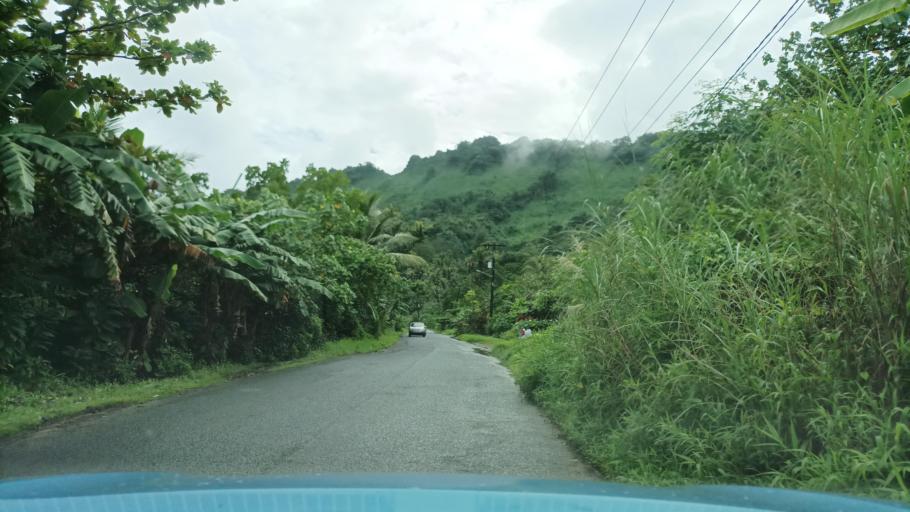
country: FM
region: Pohnpei
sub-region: Kolonia Municipality
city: Kolonia
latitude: 6.9558
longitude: 158.2472
